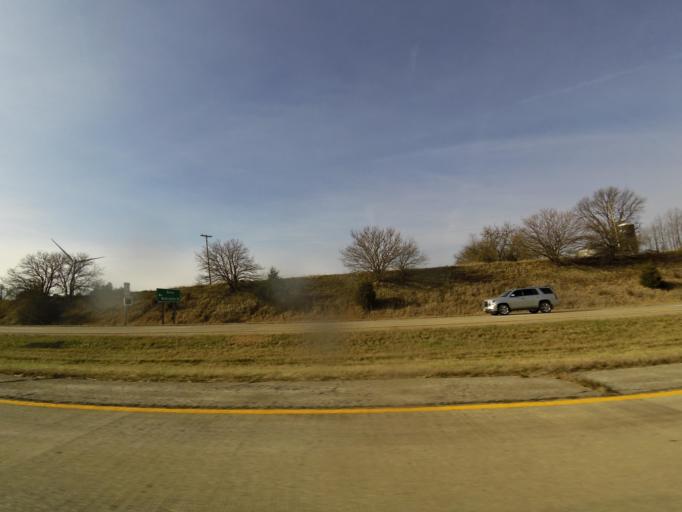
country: US
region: Illinois
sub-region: Macon County
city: Maroa
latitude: 40.0392
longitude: -88.9652
